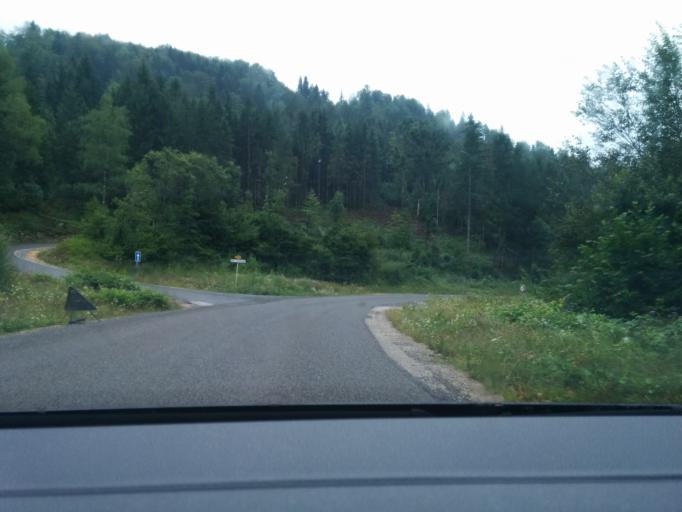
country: FR
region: Franche-Comte
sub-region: Departement du Jura
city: Saint-Lupicin
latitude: 46.4339
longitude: 5.8131
